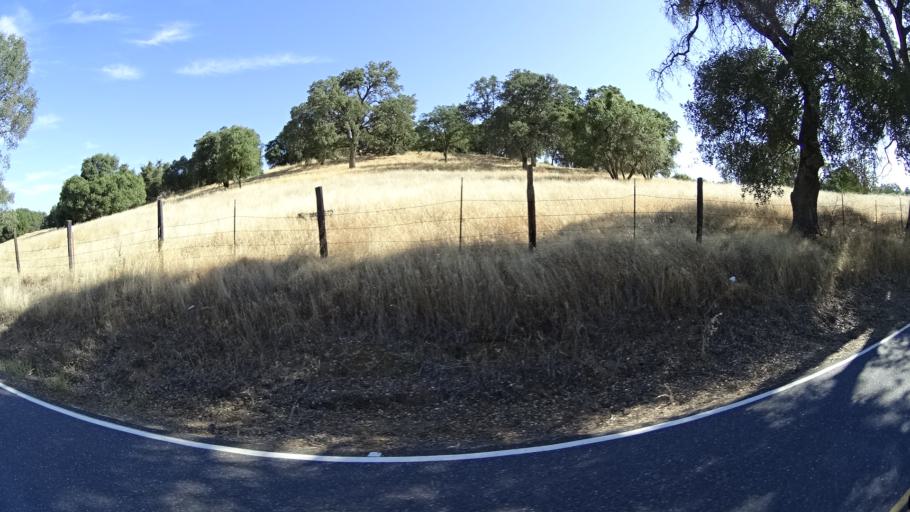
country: US
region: California
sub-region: Calaveras County
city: San Andreas
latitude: 38.1515
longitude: -120.6051
